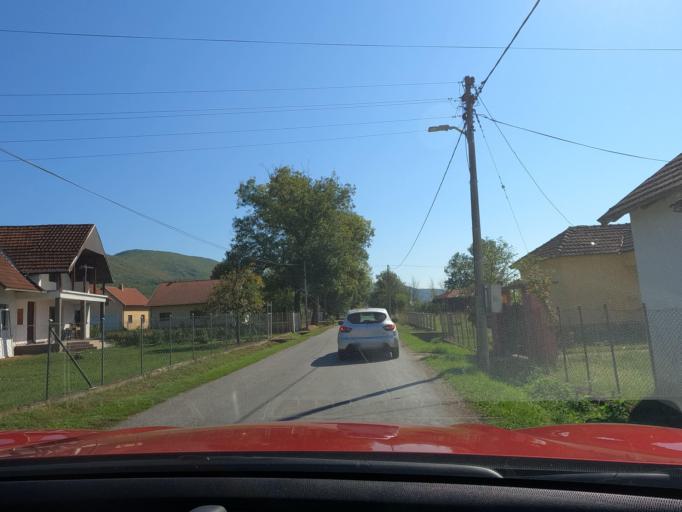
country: RS
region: Central Serbia
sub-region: Raski Okrug
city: Kraljevo
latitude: 43.7497
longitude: 20.7110
